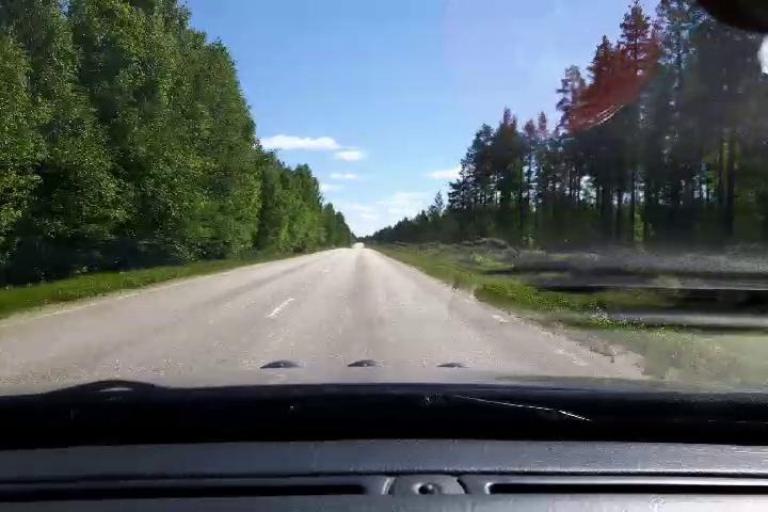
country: SE
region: Jaemtland
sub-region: Harjedalens Kommun
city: Sveg
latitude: 62.0998
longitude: 15.0744
